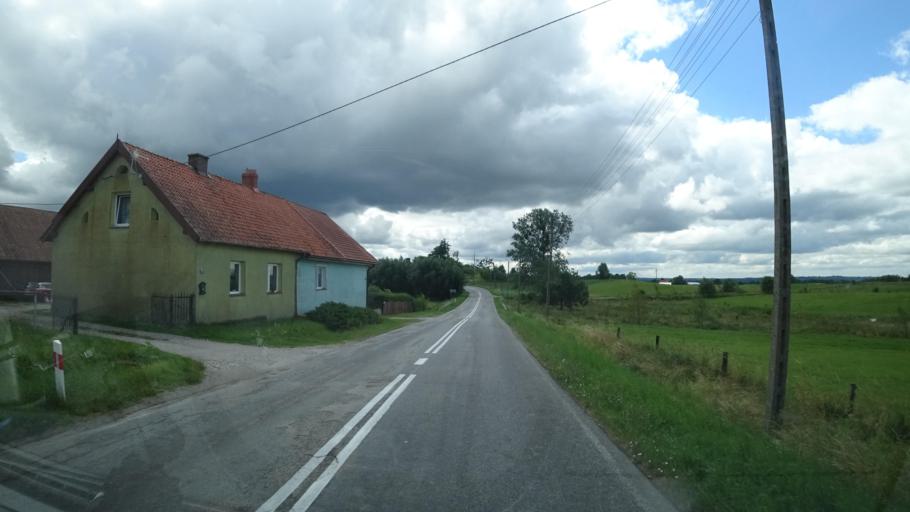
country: PL
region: Warmian-Masurian Voivodeship
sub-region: Powiat goldapski
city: Goldap
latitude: 54.2213
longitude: 22.2318
